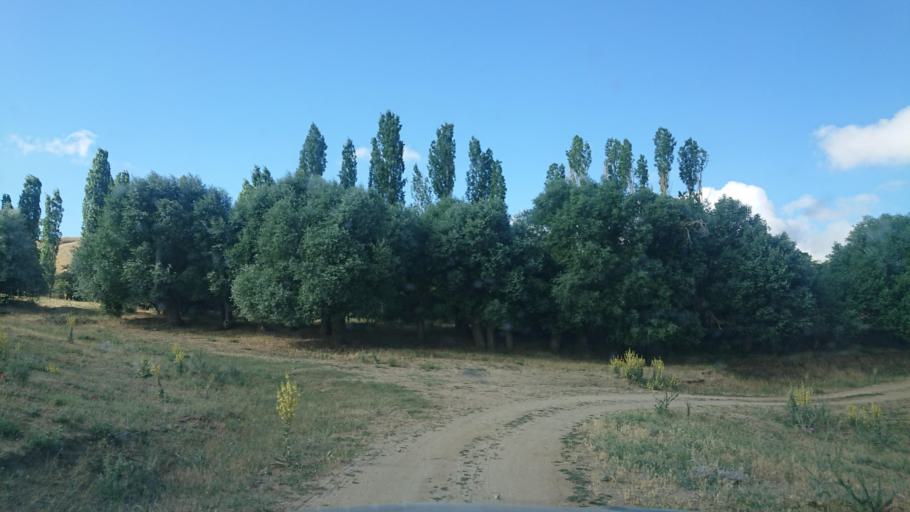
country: TR
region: Aksaray
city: Agacoren
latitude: 38.8524
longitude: 33.9356
